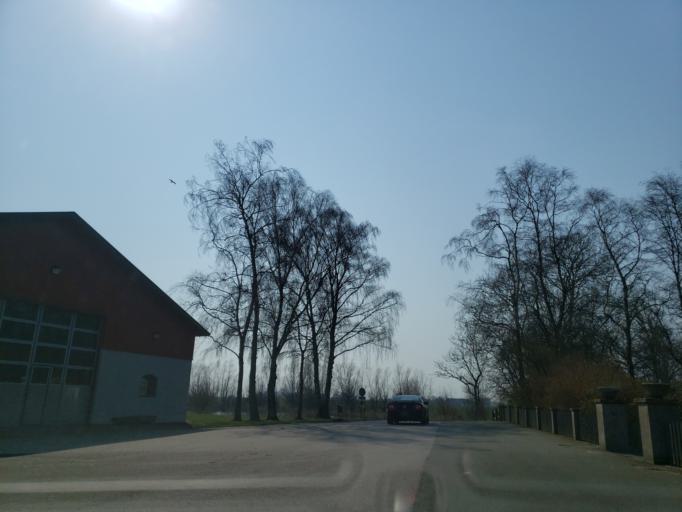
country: SE
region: Skane
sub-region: Simrishamns Kommun
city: Simrishamn
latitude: 55.5003
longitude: 14.2301
